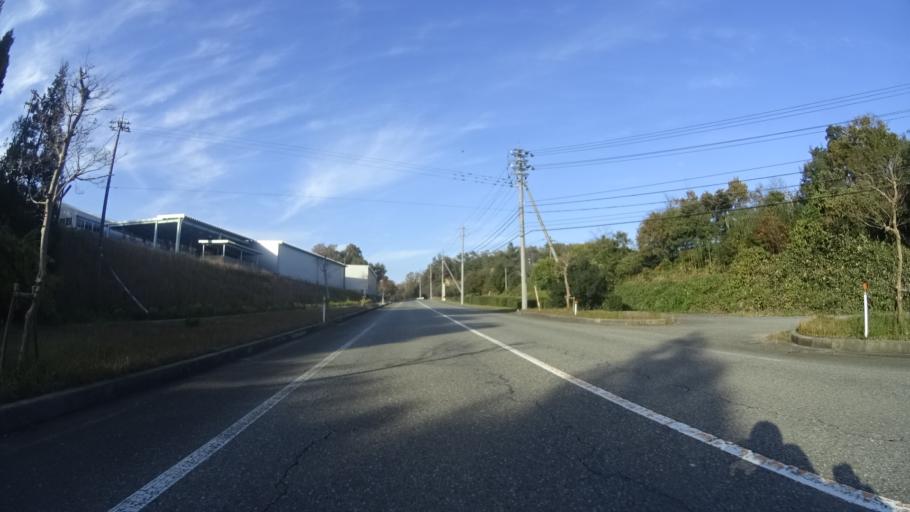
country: JP
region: Ishikawa
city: Hakui
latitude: 37.0358
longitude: 136.7786
